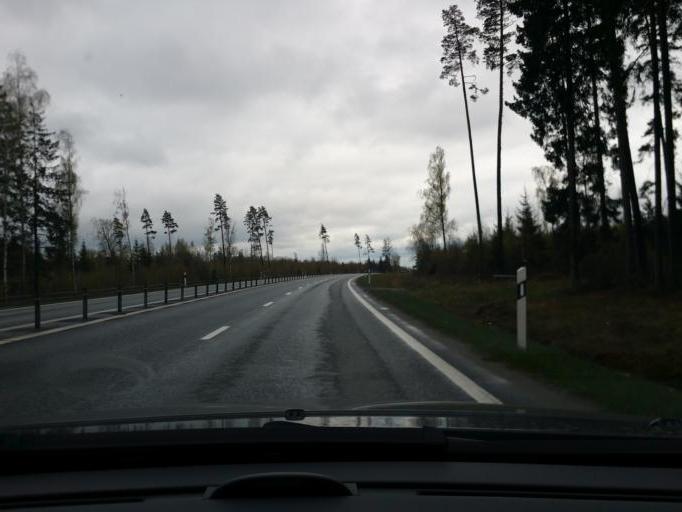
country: SE
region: Kronoberg
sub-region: Vaxjo Kommun
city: Vaexjoe
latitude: 56.9069
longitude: 14.7267
